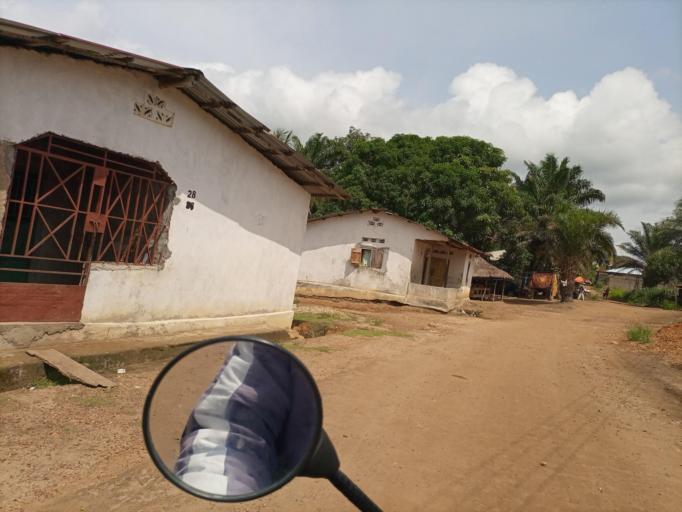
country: SL
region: Southern Province
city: Bo
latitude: 7.9715
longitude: -11.7654
